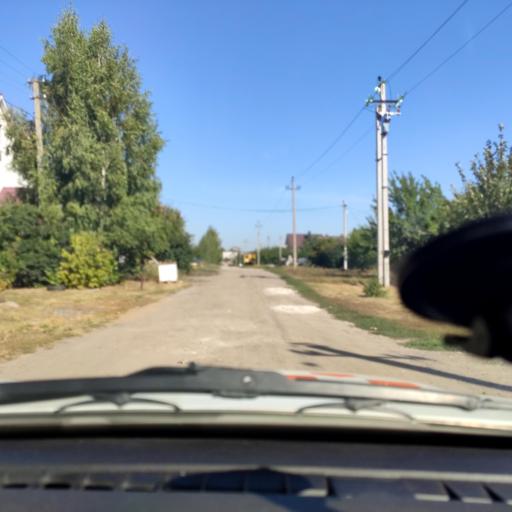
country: RU
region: Voronezj
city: Novaya Usman'
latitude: 51.6417
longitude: 39.3359
